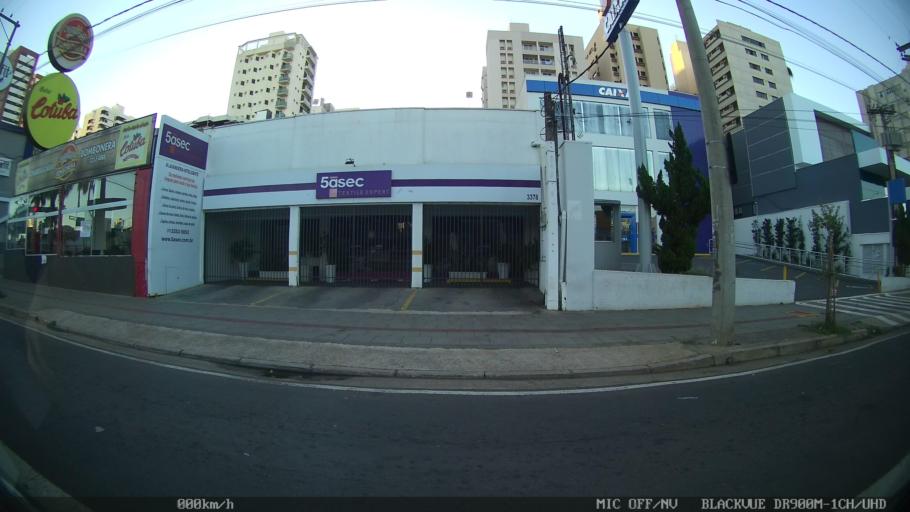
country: BR
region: Sao Paulo
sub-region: Sao Jose Do Rio Preto
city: Sao Jose do Rio Preto
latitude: -20.8162
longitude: -49.3807
